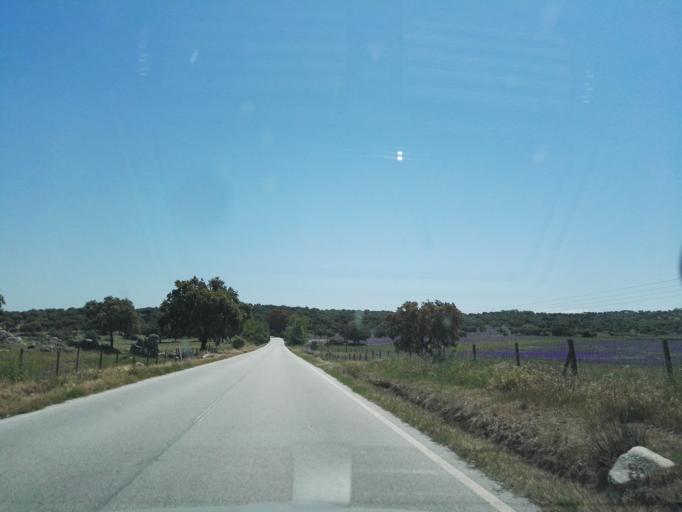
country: PT
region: Portalegre
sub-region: Arronches
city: Arronches
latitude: 39.0033
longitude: -7.2258
